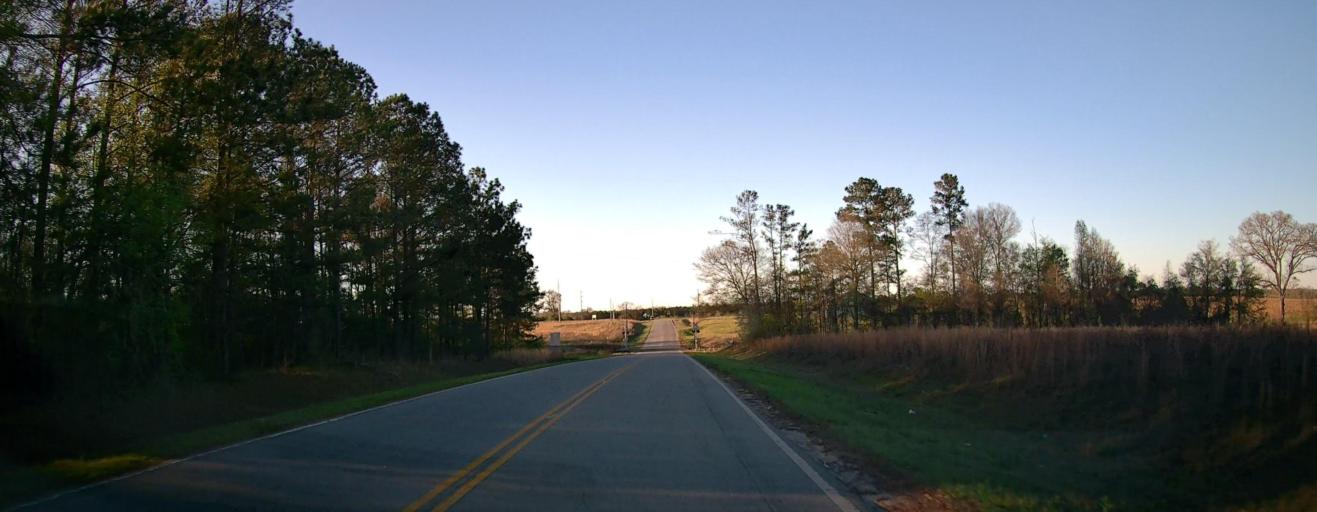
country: US
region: Georgia
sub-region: Wilkinson County
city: Gordon
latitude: 32.8927
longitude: -83.3011
